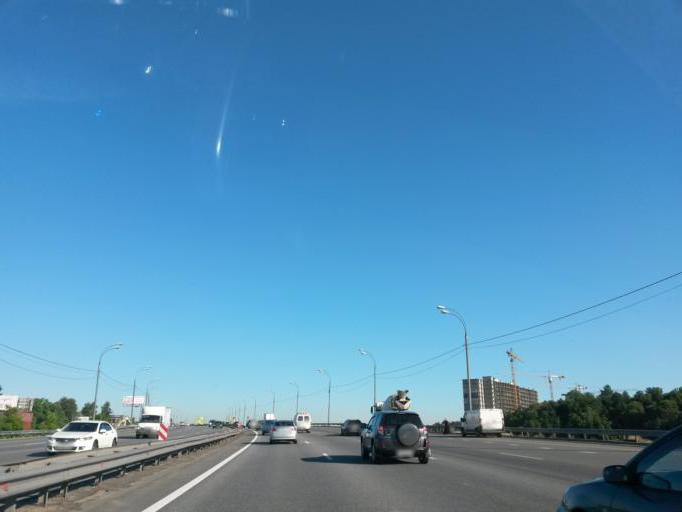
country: RU
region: Moskovskaya
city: Vidnoye
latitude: 55.5465
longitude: 37.6922
